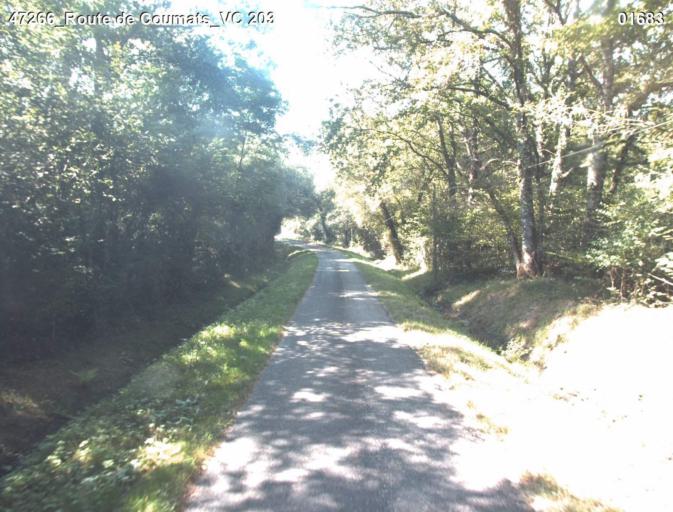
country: FR
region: Aquitaine
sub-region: Departement des Landes
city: Gabarret
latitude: 44.0046
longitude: 0.0963
